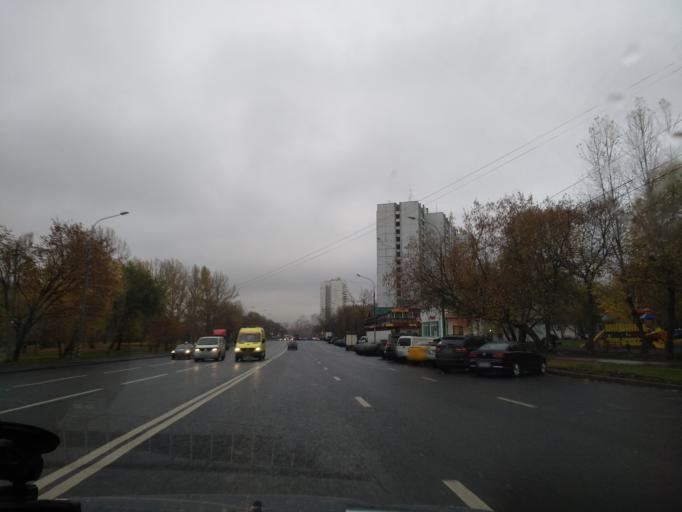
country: RU
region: Moscow
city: Kozeyevo
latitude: 55.8717
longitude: 37.6179
